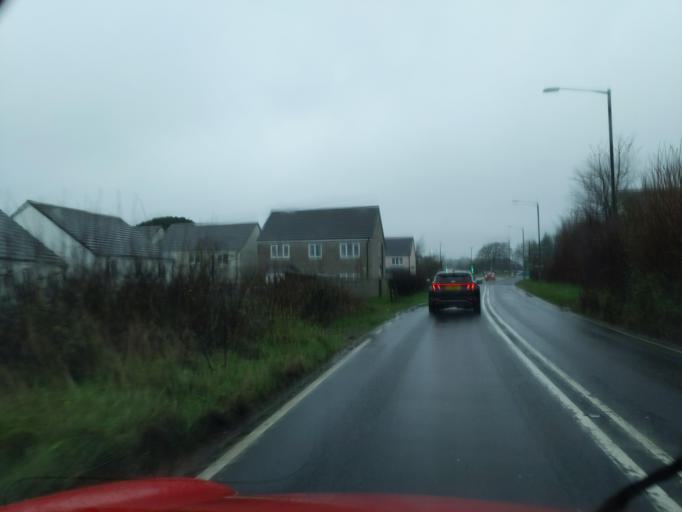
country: GB
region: England
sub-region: Cornwall
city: Launceston
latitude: 50.6278
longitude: -4.3451
